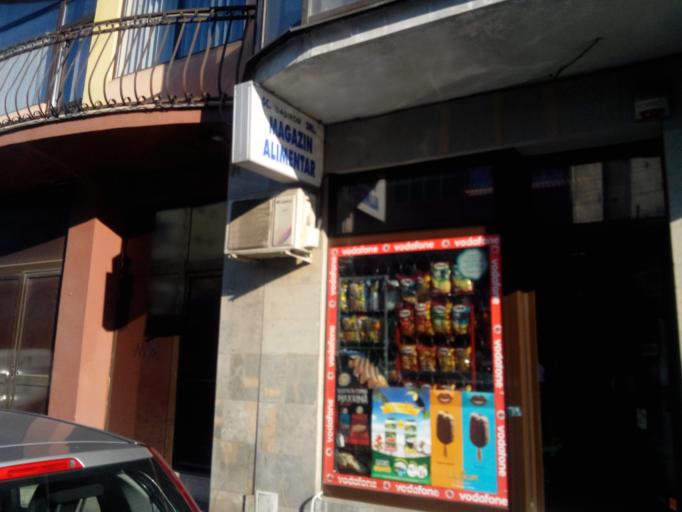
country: RO
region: Cluj
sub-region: Municipiul Cluj-Napoca
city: Cluj-Napoca
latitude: 46.7812
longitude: 23.6082
